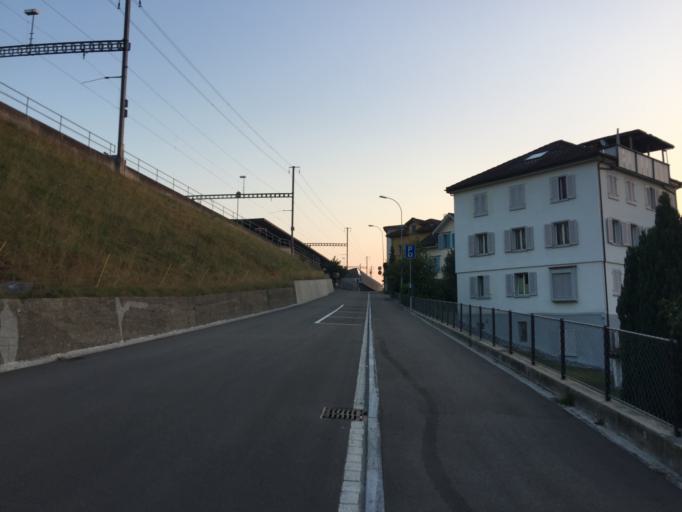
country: CH
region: Saint Gallen
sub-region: Wahlkreis Wil
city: Oberuzwil
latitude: 47.4353
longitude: 9.1311
